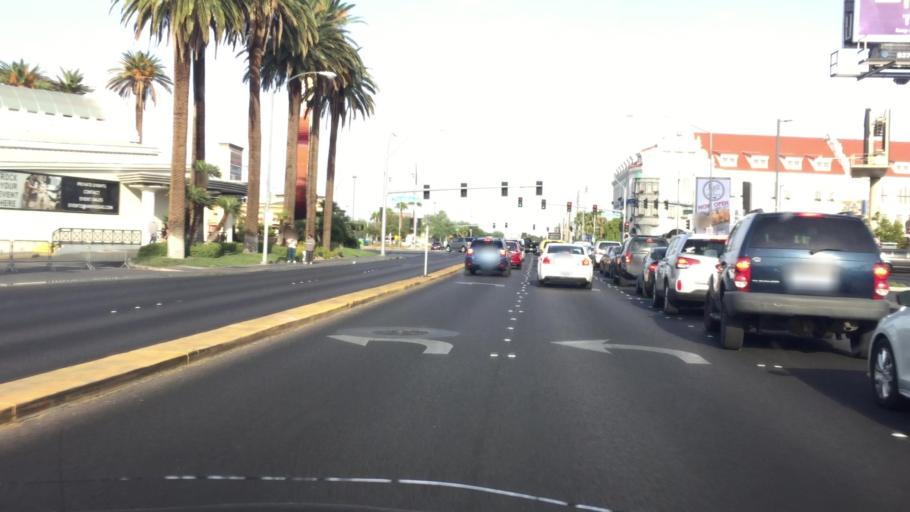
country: US
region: Nevada
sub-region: Clark County
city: Paradise
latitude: 36.1080
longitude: -115.1532
